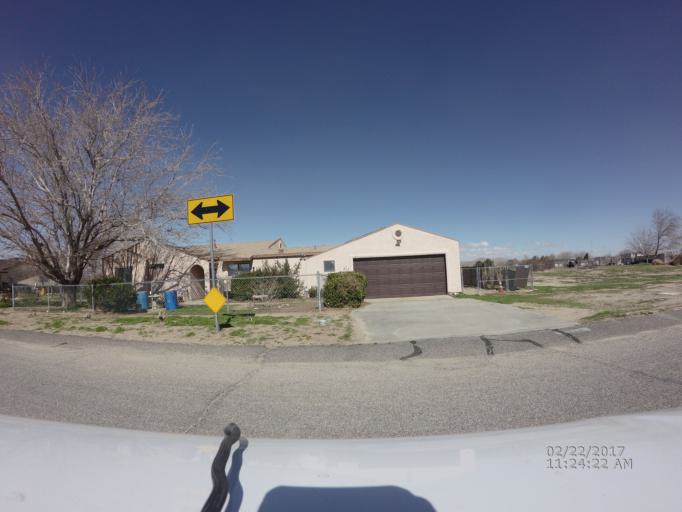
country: US
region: California
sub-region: Los Angeles County
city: Lake Los Angeles
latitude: 34.6230
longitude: -117.8127
